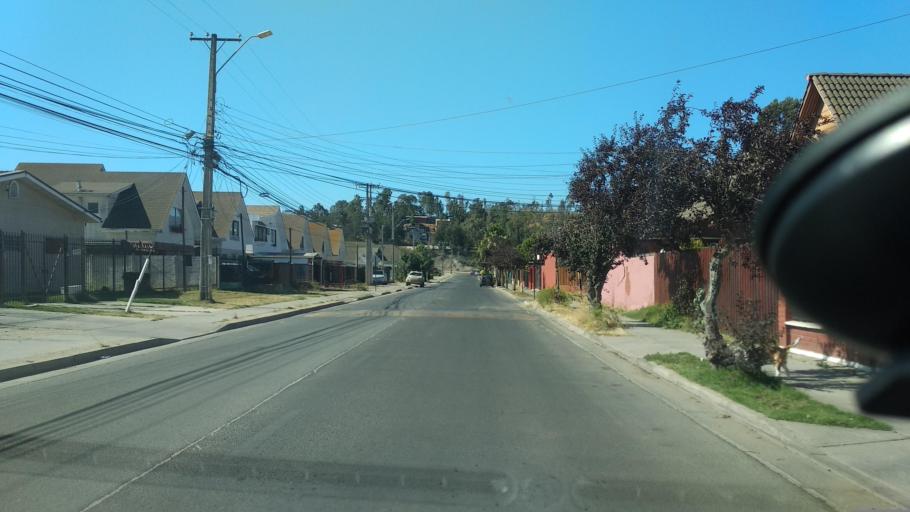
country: CL
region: Valparaiso
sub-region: Provincia de Marga Marga
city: Villa Alemana
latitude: -33.0412
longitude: -71.3904
